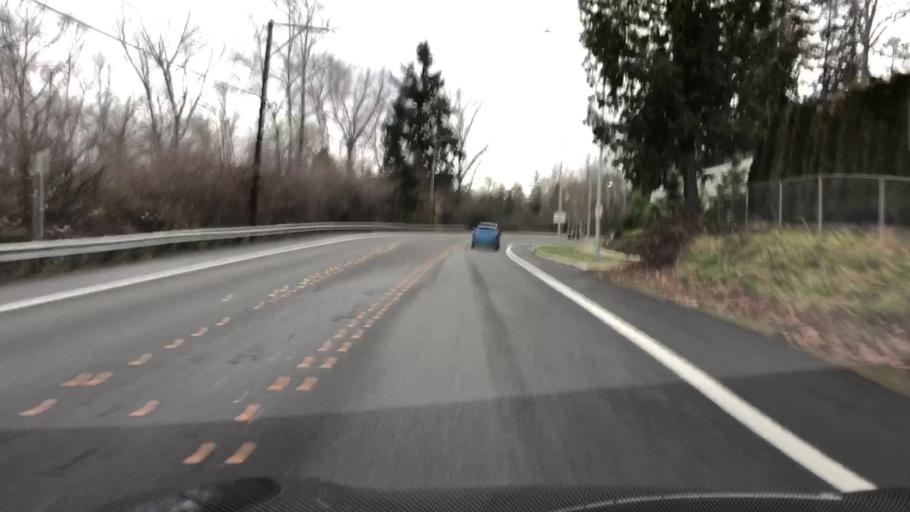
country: US
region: Washington
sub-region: King County
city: Sammamish
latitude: 47.6557
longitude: -122.0925
